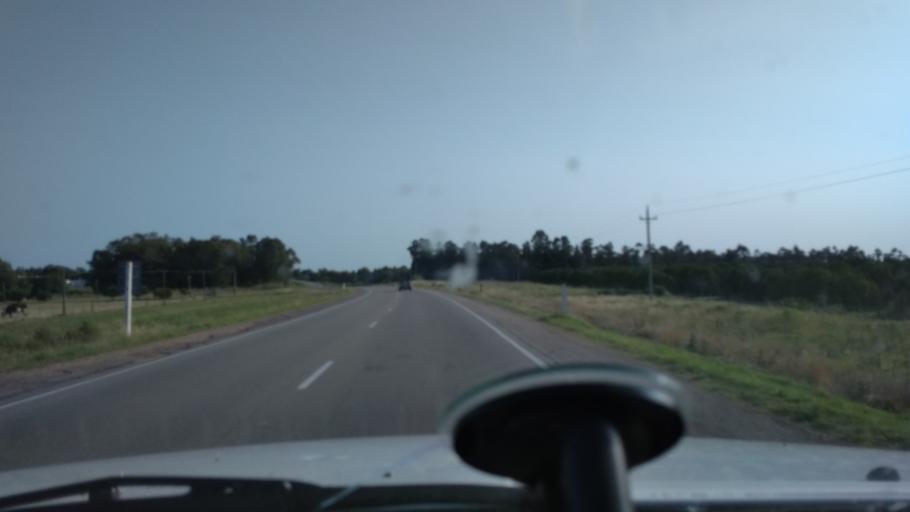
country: UY
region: Canelones
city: Sauce
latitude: -34.5727
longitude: -56.0570
